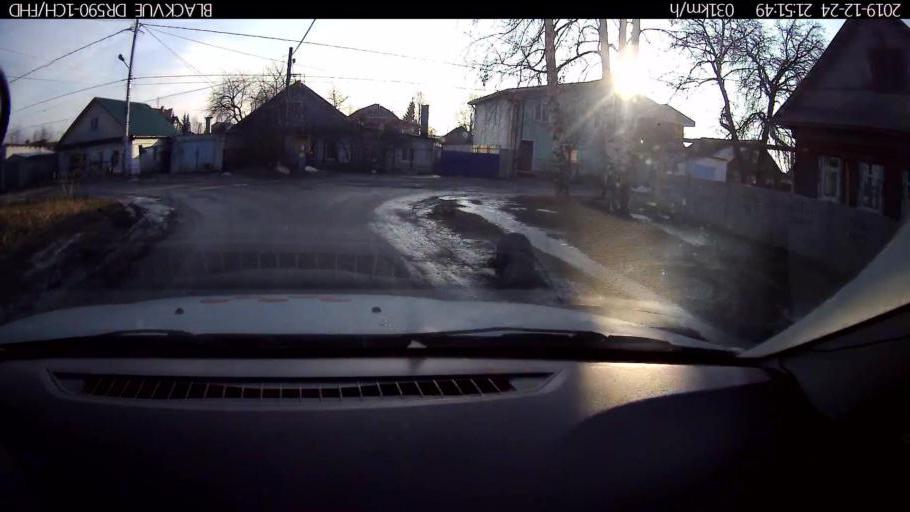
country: RU
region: Nizjnij Novgorod
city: Burevestnik
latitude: 56.2182
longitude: 43.8438
